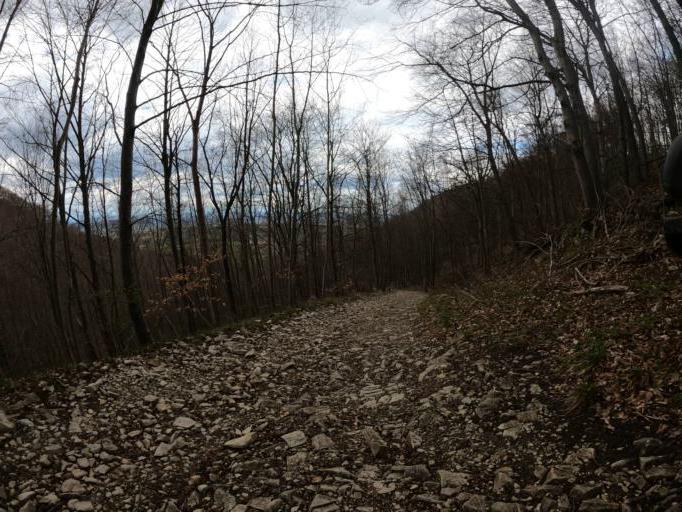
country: DE
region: Baden-Wuerttemberg
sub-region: Tuebingen Region
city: Gomaringen
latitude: 48.4026
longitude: 9.1182
